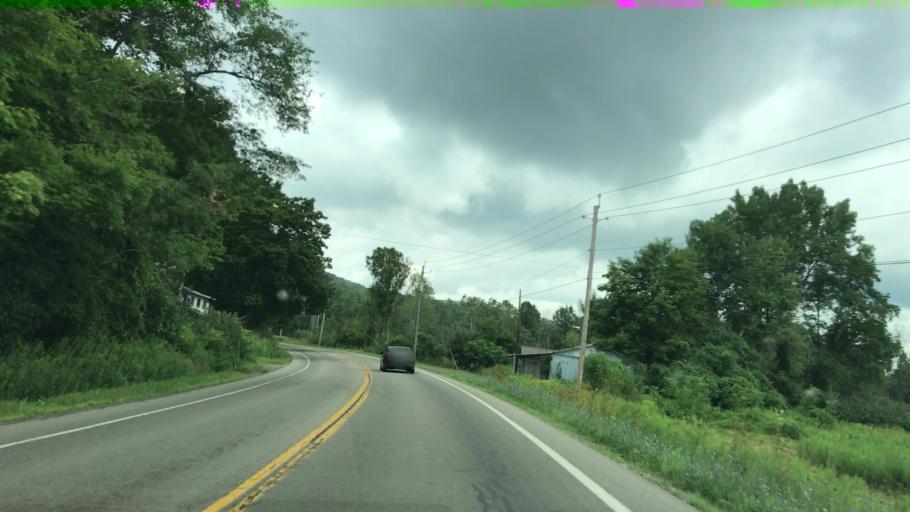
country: US
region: New York
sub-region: Steuben County
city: Bath
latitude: 42.4015
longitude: -77.3493
